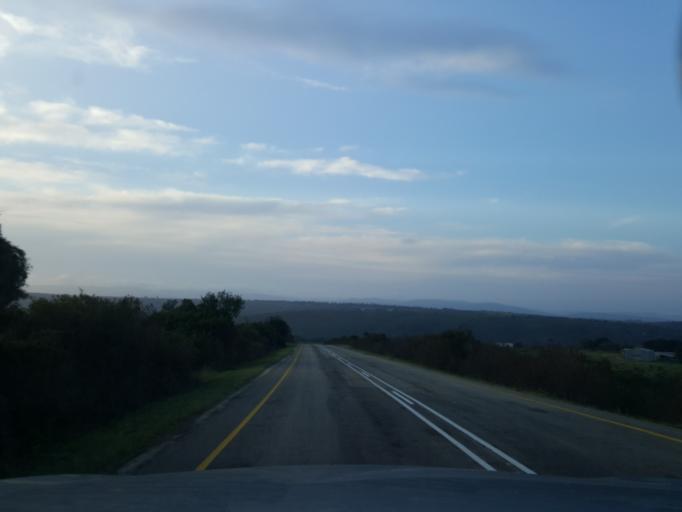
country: ZA
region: Eastern Cape
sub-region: Cacadu District Municipality
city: Grahamstown
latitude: -33.4833
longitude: 26.4895
